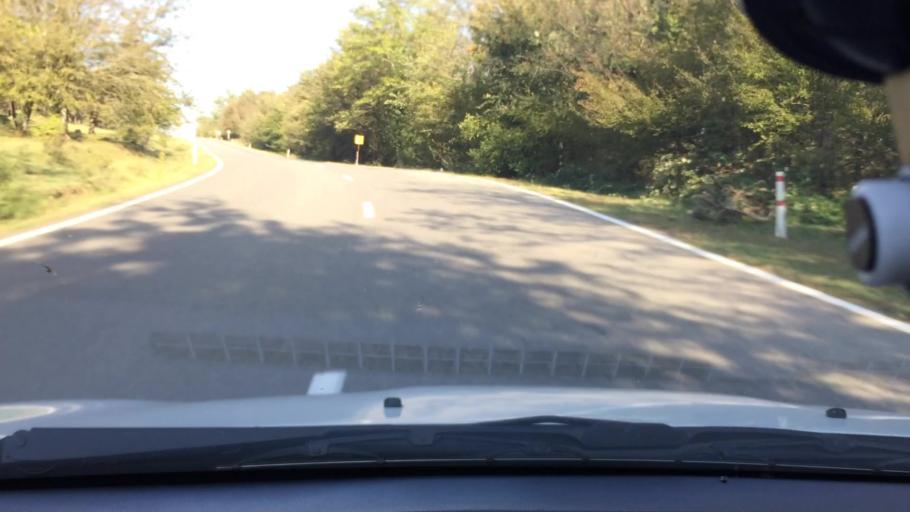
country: GE
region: Imereti
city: Kutaisi
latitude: 42.2500
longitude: 42.7543
